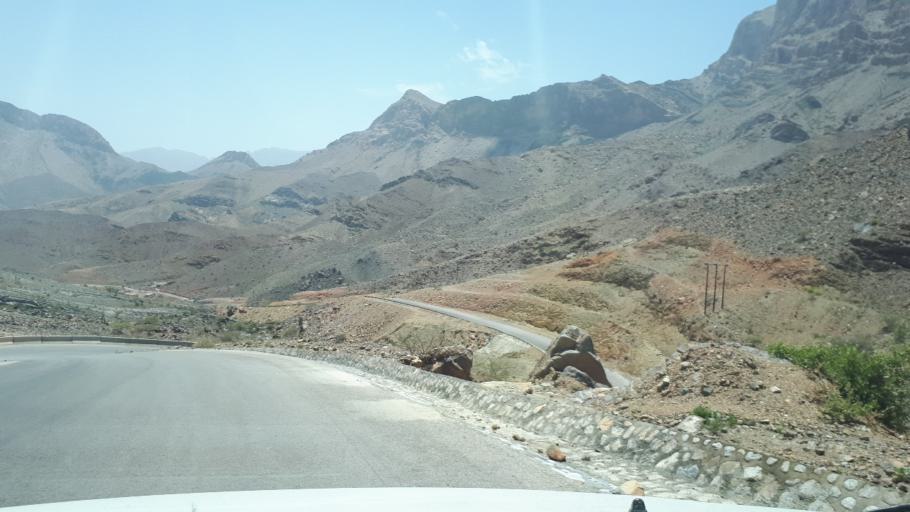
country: OM
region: Muhafazat ad Dakhiliyah
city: Bahla'
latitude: 23.2026
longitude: 57.1419
